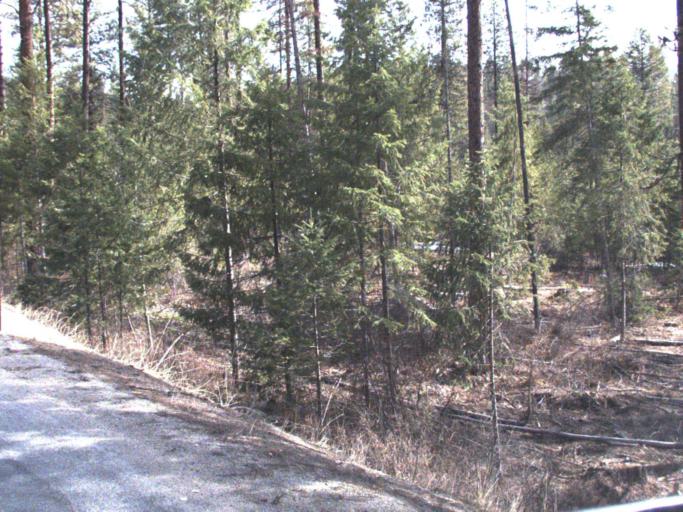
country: US
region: Washington
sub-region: Stevens County
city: Chewelah
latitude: 48.5093
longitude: -117.6635
